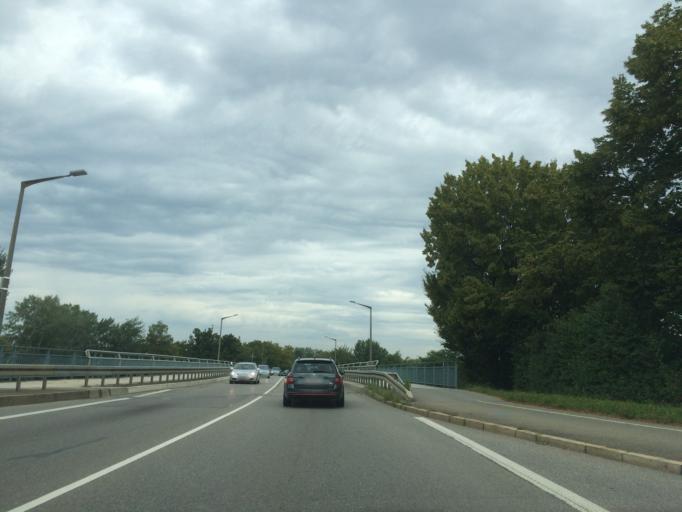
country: DE
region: Baden-Wuerttemberg
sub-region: Tuebingen Region
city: Friedrichshafen
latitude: 47.6642
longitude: 9.4302
